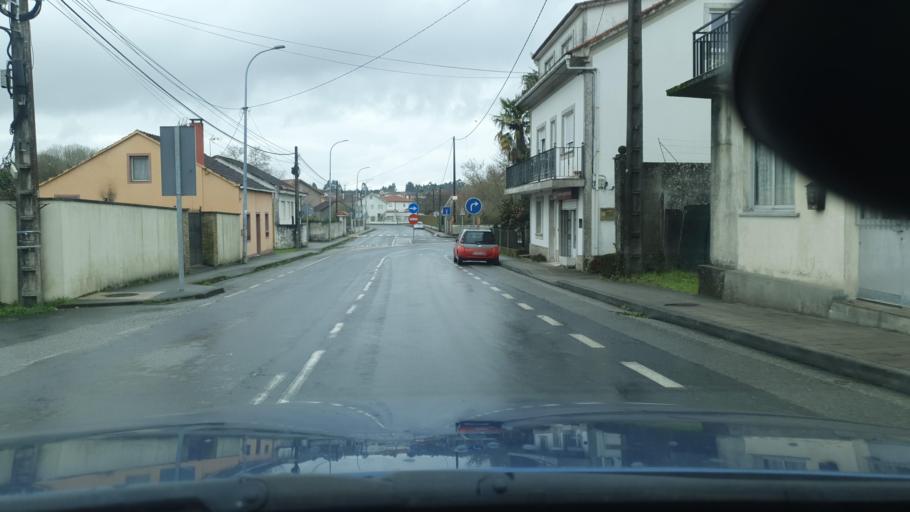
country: ES
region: Galicia
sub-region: Provincia da Coruna
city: Ames
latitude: 42.8244
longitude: -8.6127
